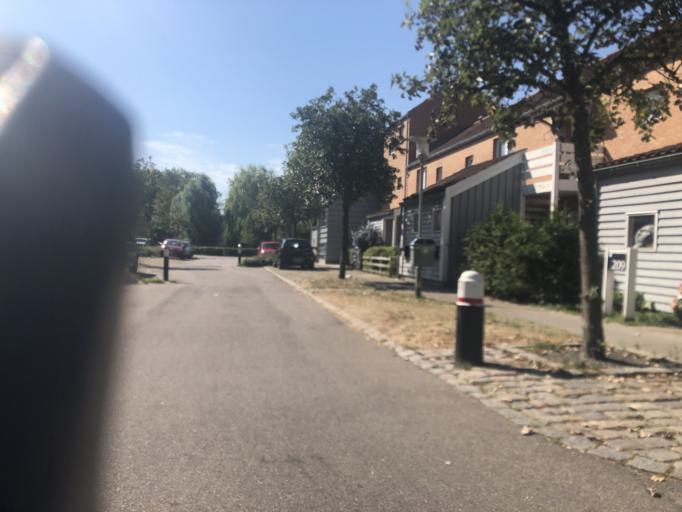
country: DK
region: Capital Region
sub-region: Gladsaxe Municipality
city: Buddinge
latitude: 55.7427
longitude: 12.4743
